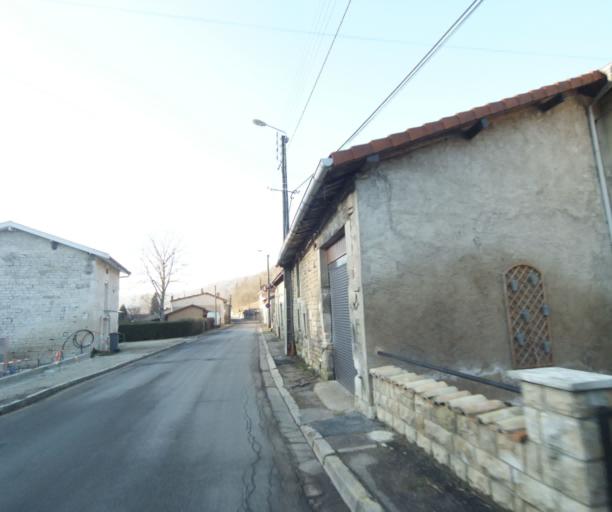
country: FR
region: Champagne-Ardenne
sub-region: Departement de la Haute-Marne
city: Chevillon
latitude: 48.5276
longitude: 5.1435
